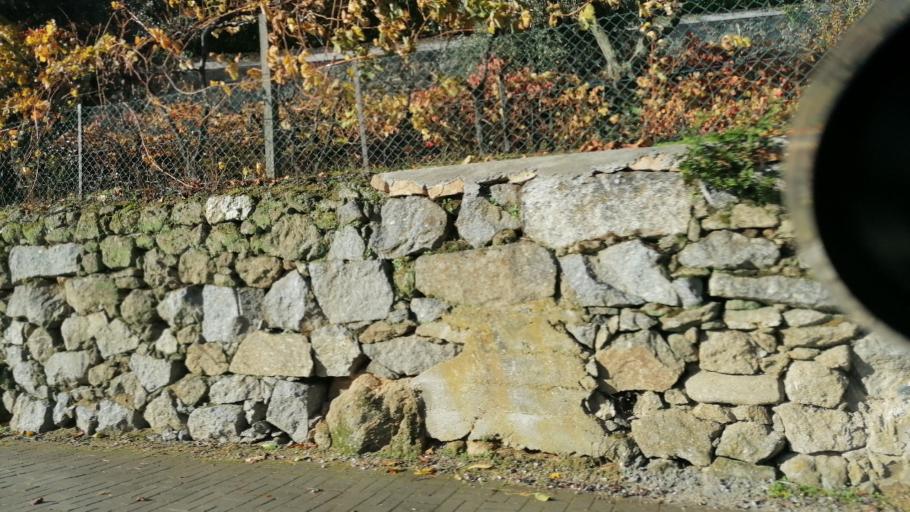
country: PT
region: Viseu
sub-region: Lamego
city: Lamego
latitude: 41.0992
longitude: -7.8010
